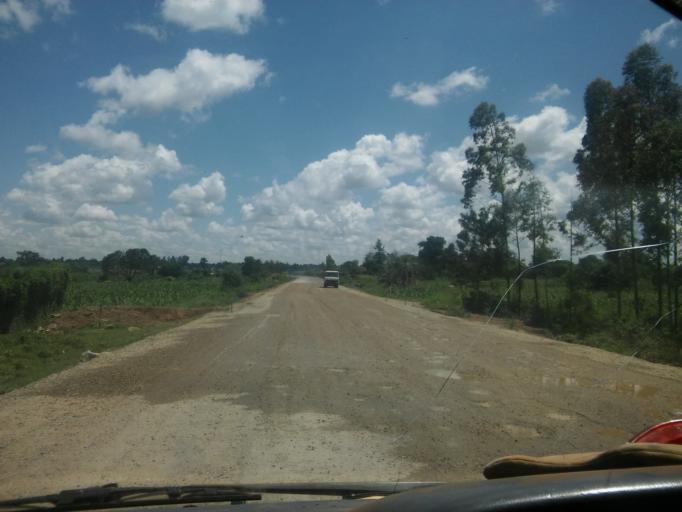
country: UG
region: Eastern Region
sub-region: Mbale District
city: Mbale
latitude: 1.0749
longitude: 34.1129
